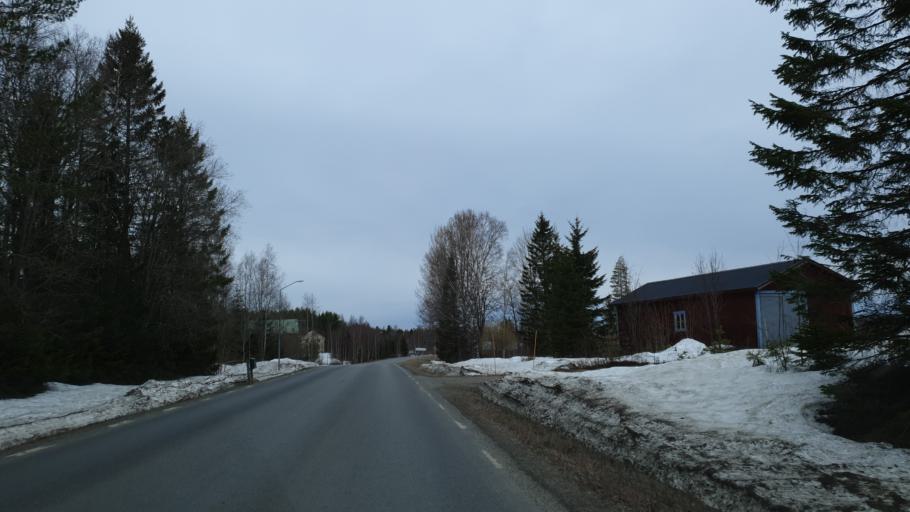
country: SE
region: Vaesterbotten
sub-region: Robertsfors Kommun
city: Robertsfors
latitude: 64.3776
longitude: 20.9012
